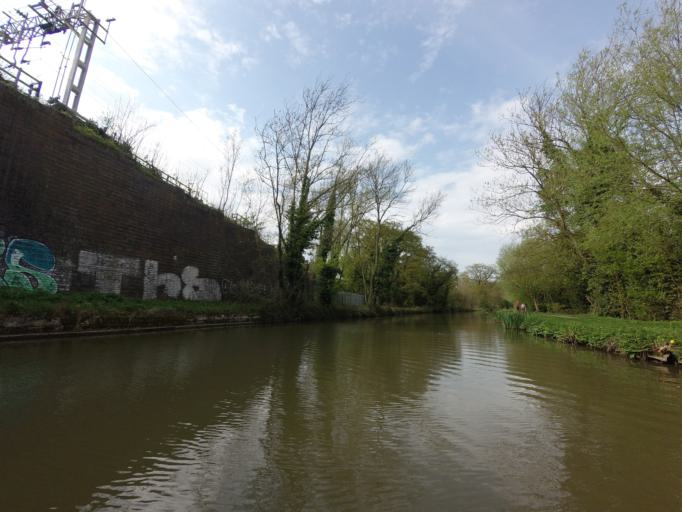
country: GB
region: England
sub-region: Central Bedfordshire
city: Leighton Buzzard
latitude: 51.9282
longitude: -0.6774
